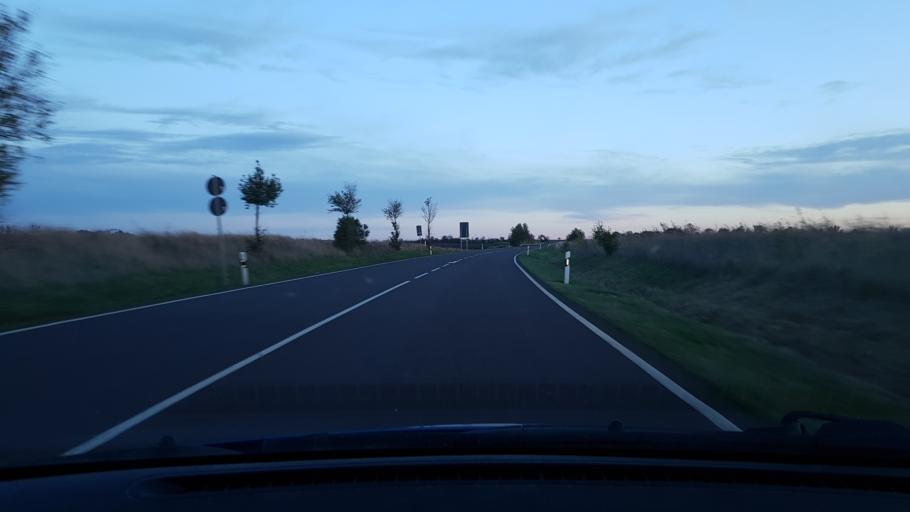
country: DE
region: Saxony-Anhalt
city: Leitzkau
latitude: 52.0579
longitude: 11.9372
